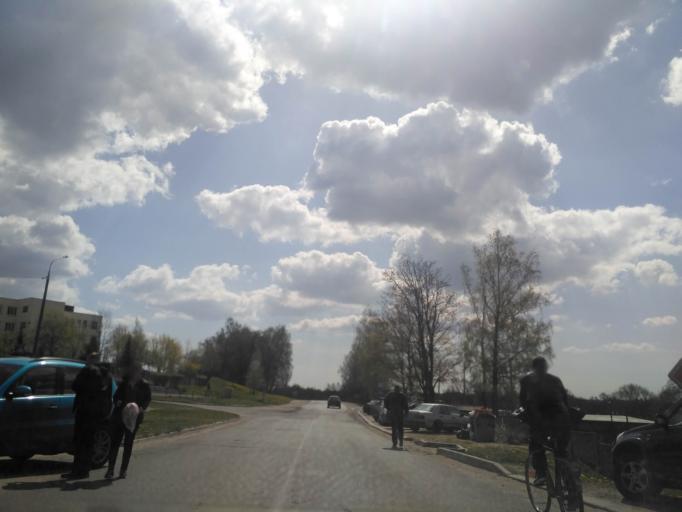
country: BY
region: Minsk
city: Radashkovichy
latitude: 54.1501
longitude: 27.2497
